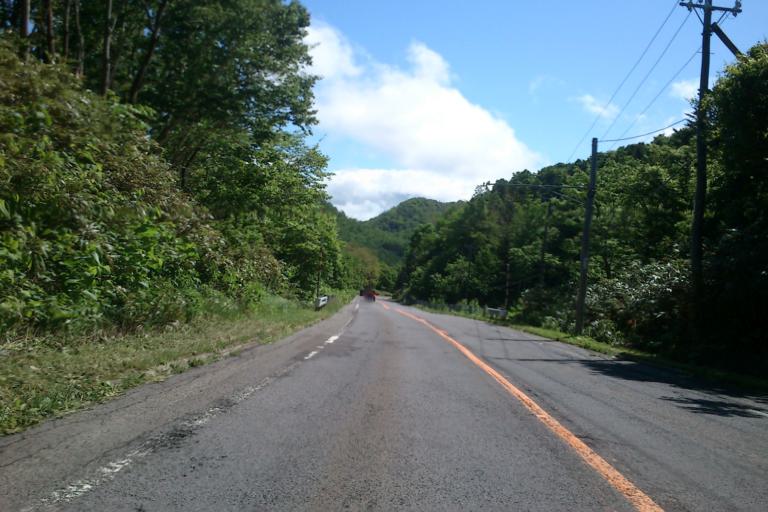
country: JP
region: Hokkaido
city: Ishikari
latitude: 43.5545
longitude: 141.3999
